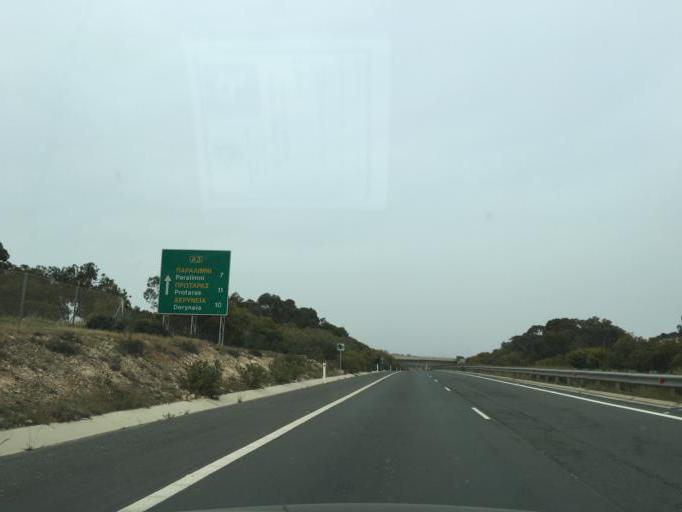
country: CY
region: Ammochostos
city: Ayia Napa
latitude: 34.9943
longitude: 33.9650
